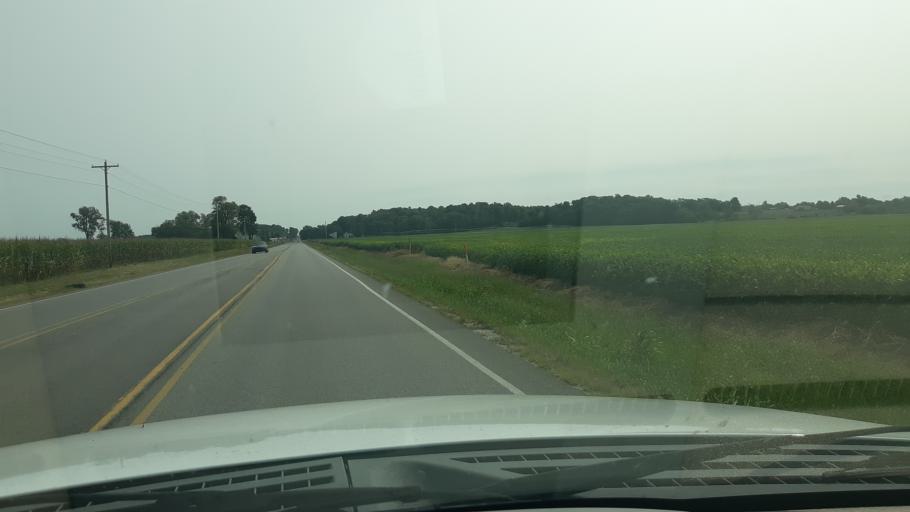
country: US
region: Indiana
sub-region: Gibson County
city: Owensville
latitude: 38.3559
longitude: -87.6835
